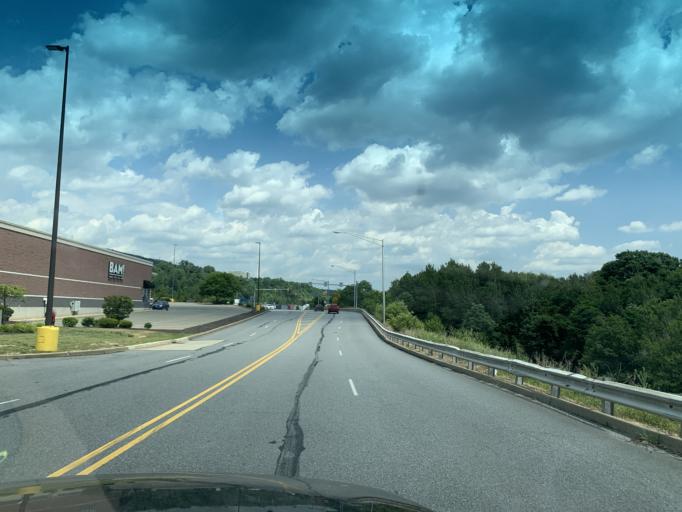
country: US
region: Pennsylvania
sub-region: Lackawanna County
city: Chinchilla
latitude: 41.4597
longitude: -75.6512
